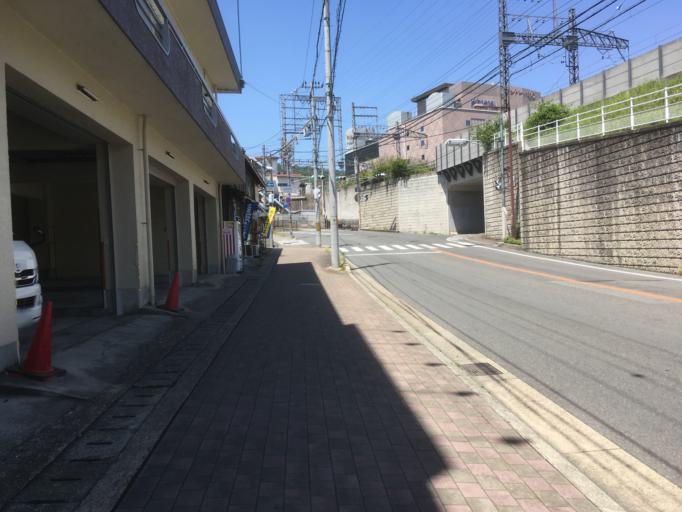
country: JP
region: Nara
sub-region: Ikoma-shi
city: Ikoma
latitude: 34.6932
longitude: 135.7006
